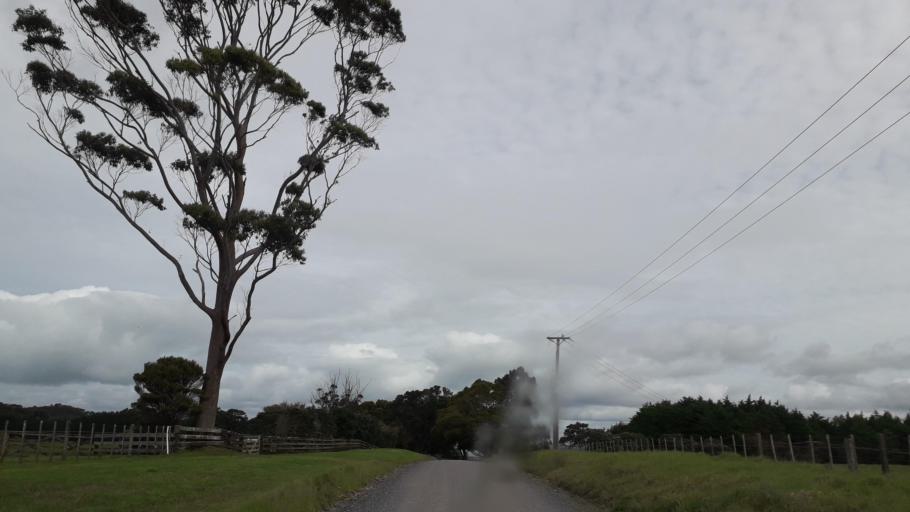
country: NZ
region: Northland
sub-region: Far North District
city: Kerikeri
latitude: -35.1508
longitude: 174.0399
